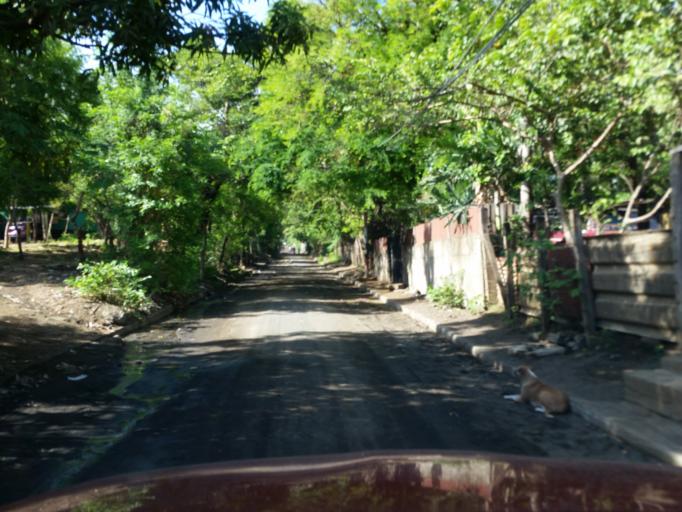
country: NI
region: Managua
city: Managua
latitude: 12.0850
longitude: -86.2612
